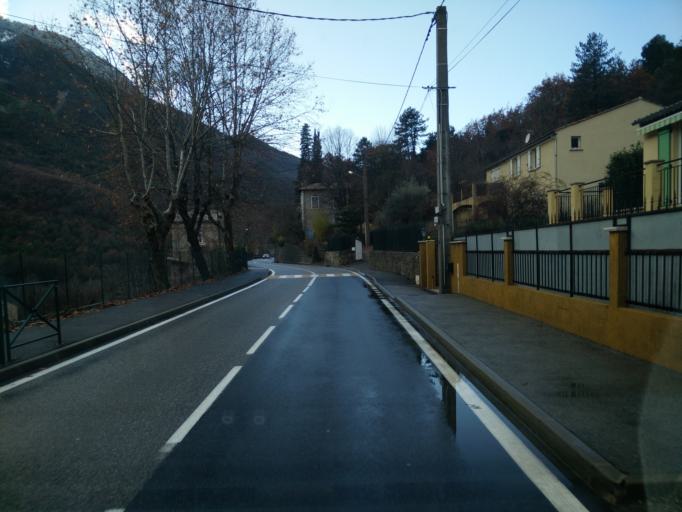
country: FR
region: Provence-Alpes-Cote d'Azur
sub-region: Departement des Alpes-Maritimes
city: Puget-Theniers
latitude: 43.9470
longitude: 7.0020
